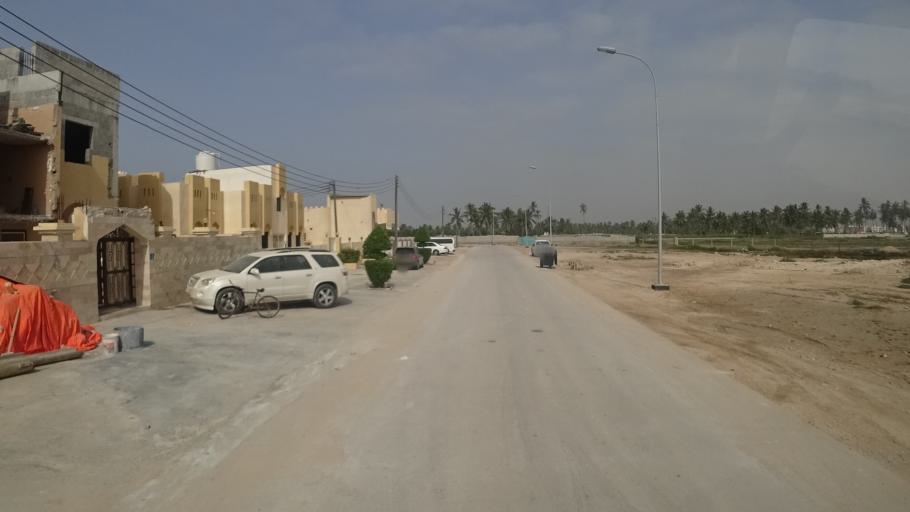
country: OM
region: Zufar
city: Salalah
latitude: 17.0160
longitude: 54.1717
